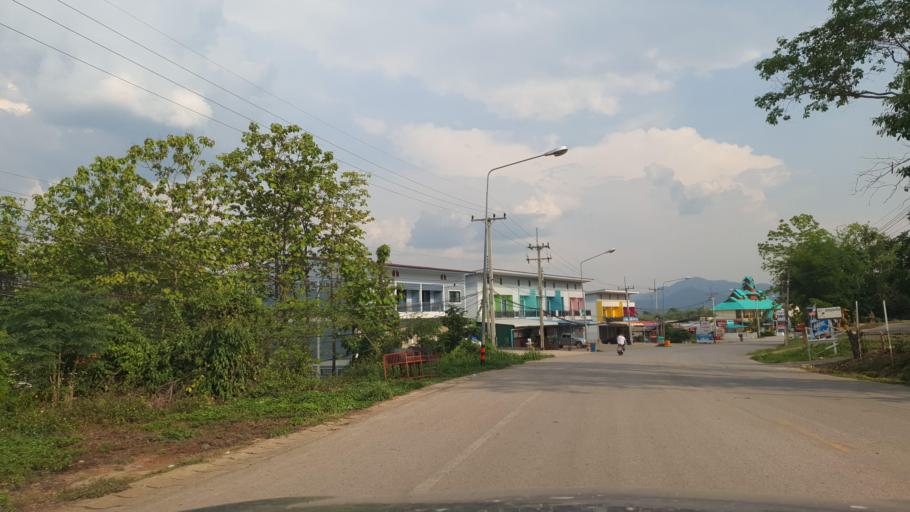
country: TH
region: Chiang Mai
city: Pai
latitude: 19.3523
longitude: 98.4351
